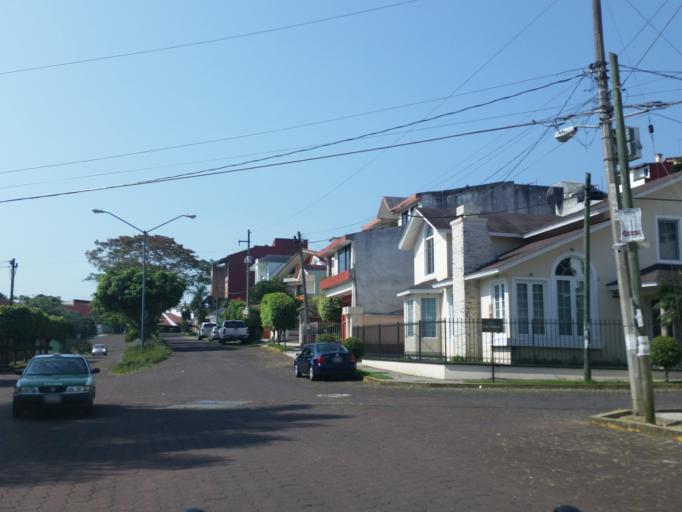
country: MX
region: Veracruz
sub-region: Xalapa
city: Xalapa de Enriquez
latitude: 19.5223
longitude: -96.9033
